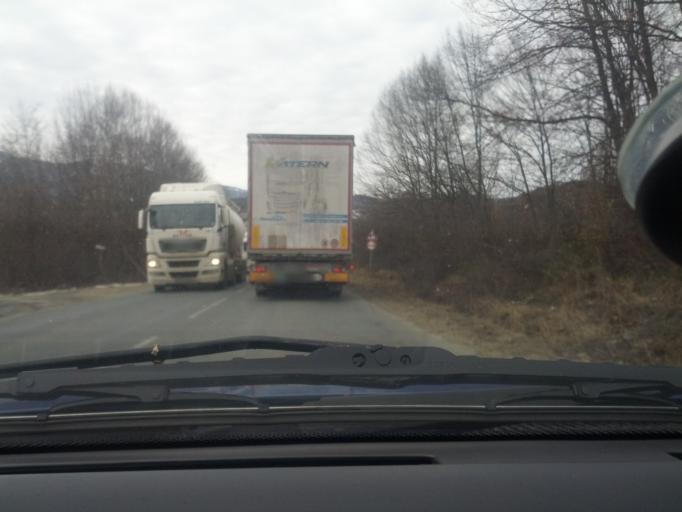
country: BG
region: Vratsa
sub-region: Obshtina Mezdra
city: Mezdra
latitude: 43.0237
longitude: 23.6719
